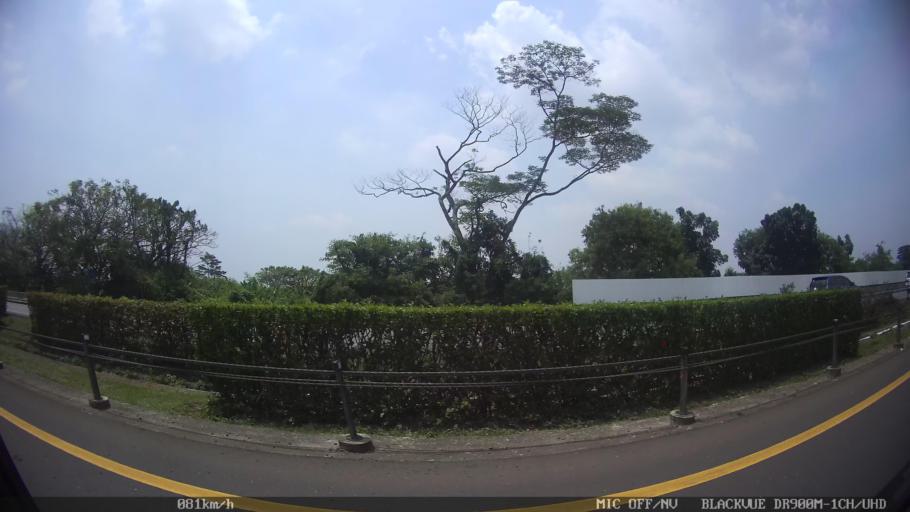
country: ID
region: West Java
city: Kresek
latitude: -6.1412
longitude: 106.2681
